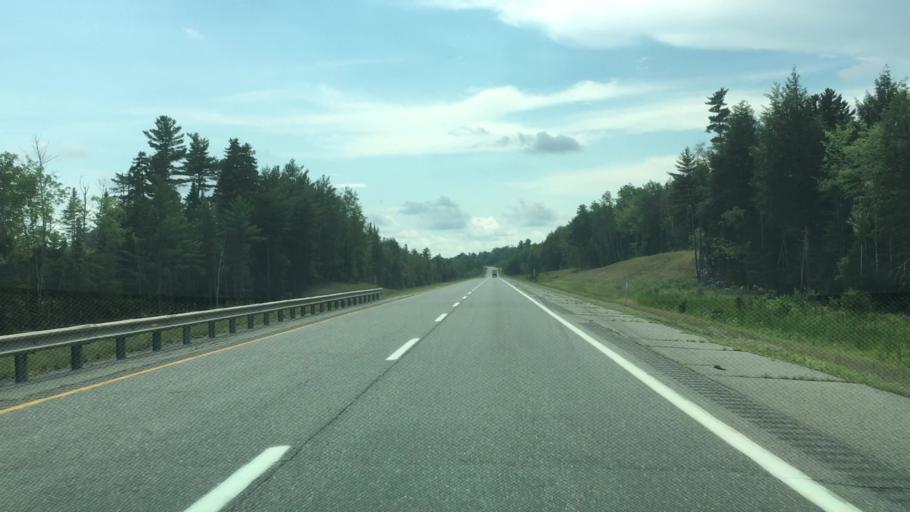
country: US
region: Maine
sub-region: Penobscot County
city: Lincoln
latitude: 45.4697
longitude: -68.5821
